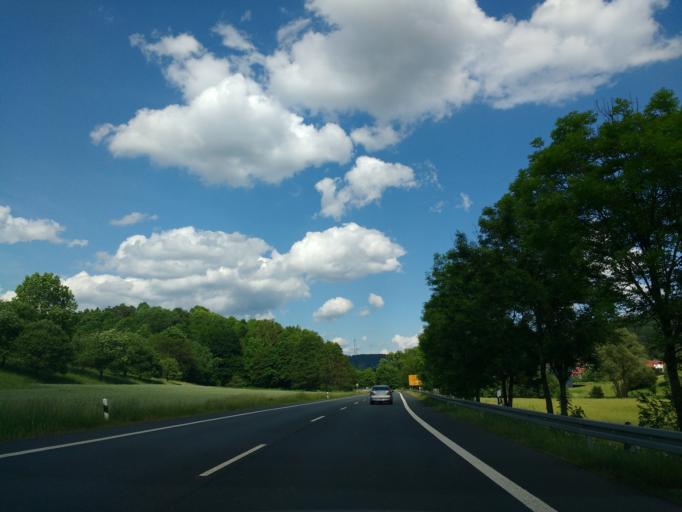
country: DE
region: Hesse
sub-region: Regierungsbezirk Giessen
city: Breidenbach
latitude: 50.8691
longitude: 8.4337
